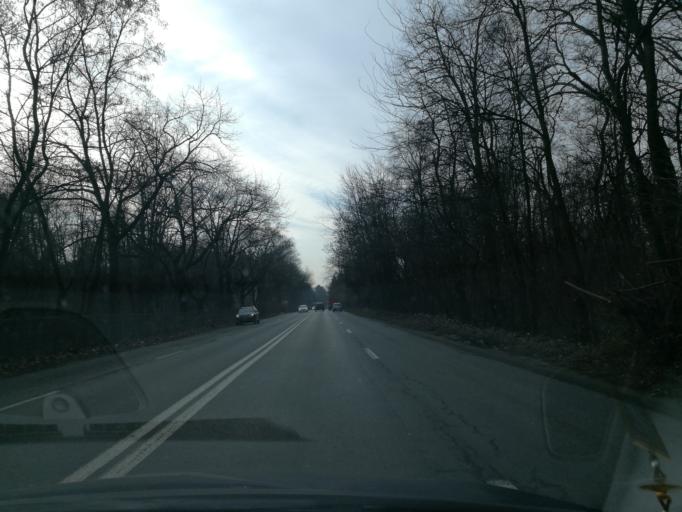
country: RO
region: Ilfov
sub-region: Voluntari City
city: Voluntari
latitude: 44.5056
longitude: 26.1837
